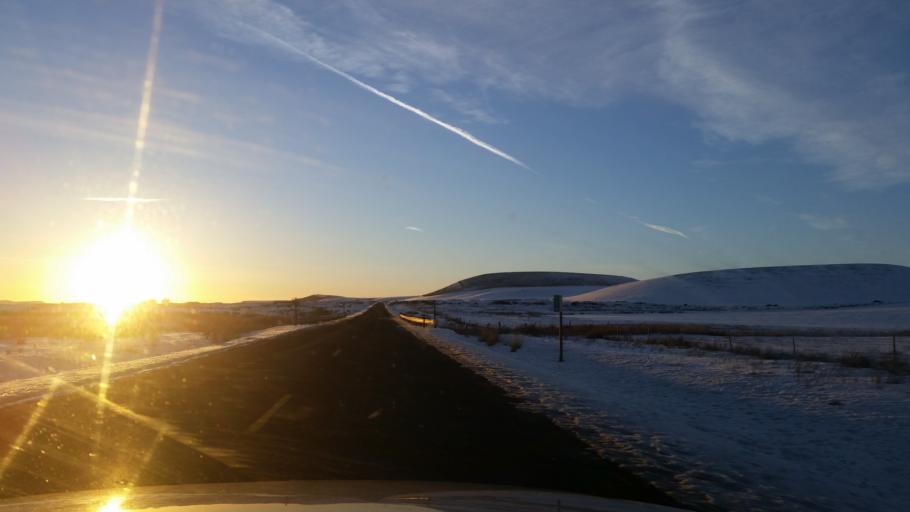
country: US
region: Washington
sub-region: Spokane County
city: Cheney
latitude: 47.1136
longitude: -117.8032
